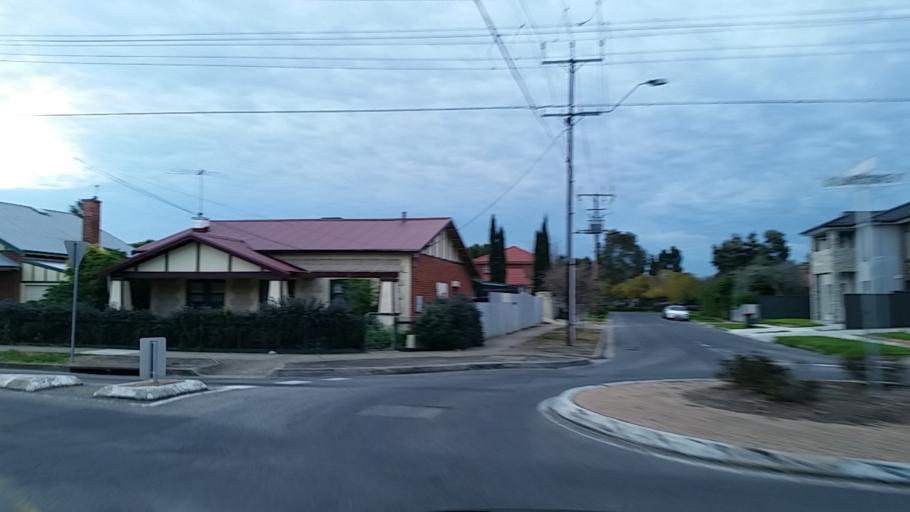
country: AU
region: South Australia
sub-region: Prospect
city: Prospect
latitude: -34.8710
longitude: 138.5905
